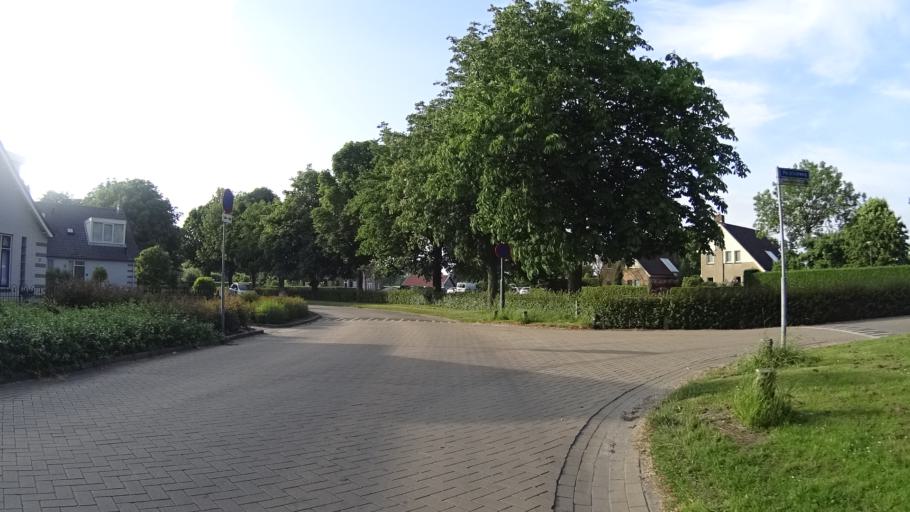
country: NL
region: North Brabant
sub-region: Gemeente Heusden
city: Heusden
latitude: 51.7262
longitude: 5.1387
